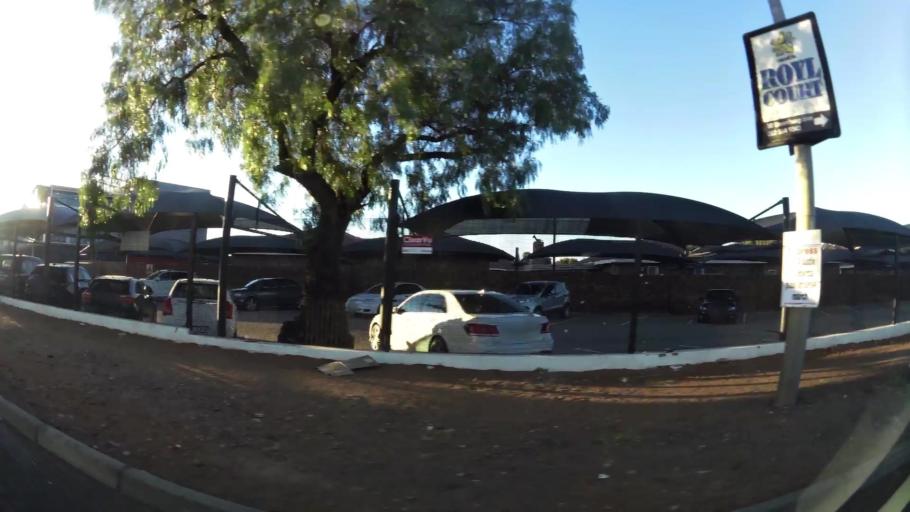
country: ZA
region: Northern Cape
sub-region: Frances Baard District Municipality
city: Kimberley
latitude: -28.7616
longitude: 24.7591
